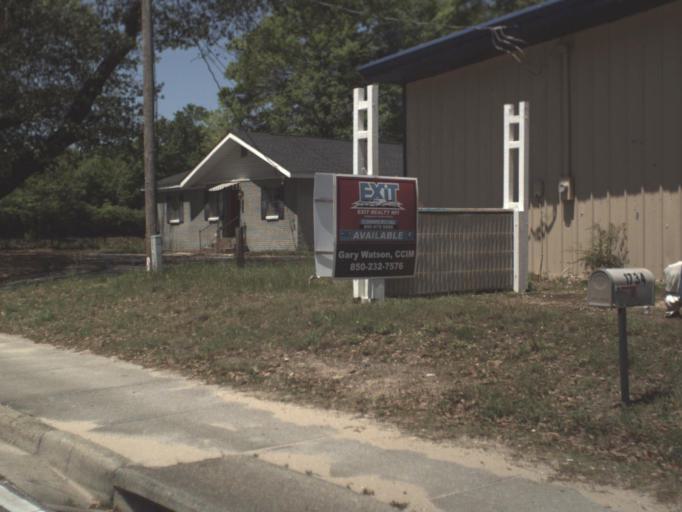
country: US
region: Florida
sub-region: Escambia County
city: Ferry Pass
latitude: 30.4956
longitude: -87.2056
